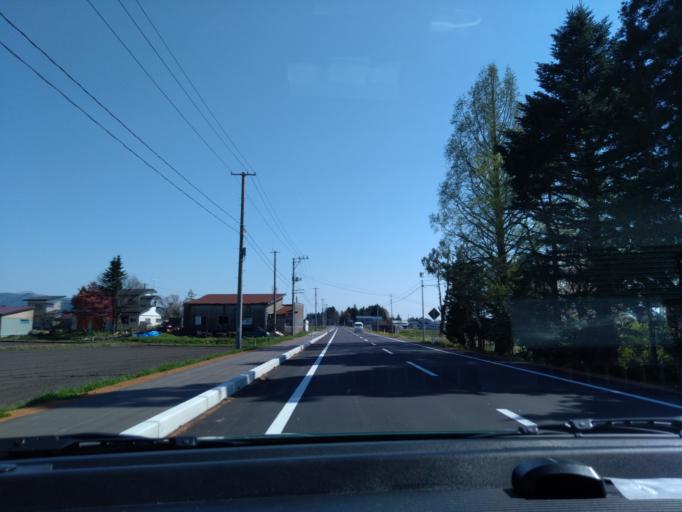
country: JP
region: Akita
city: Kakunodatemachi
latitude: 39.5369
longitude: 140.5852
